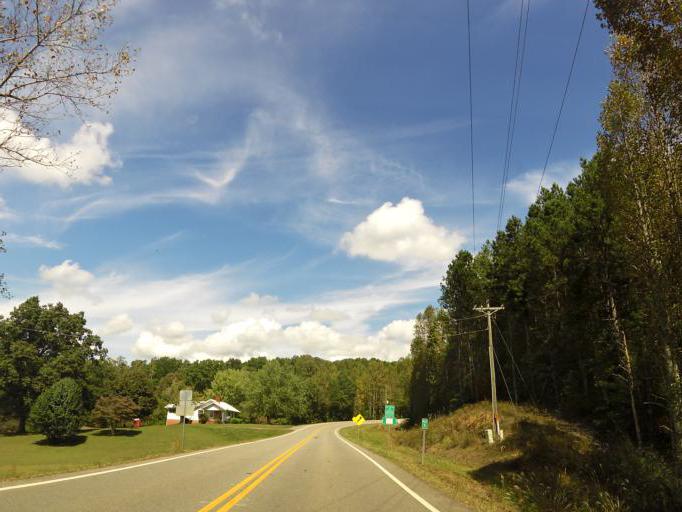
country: US
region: Georgia
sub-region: Pickens County
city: Jasper
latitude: 34.5481
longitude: -84.2604
